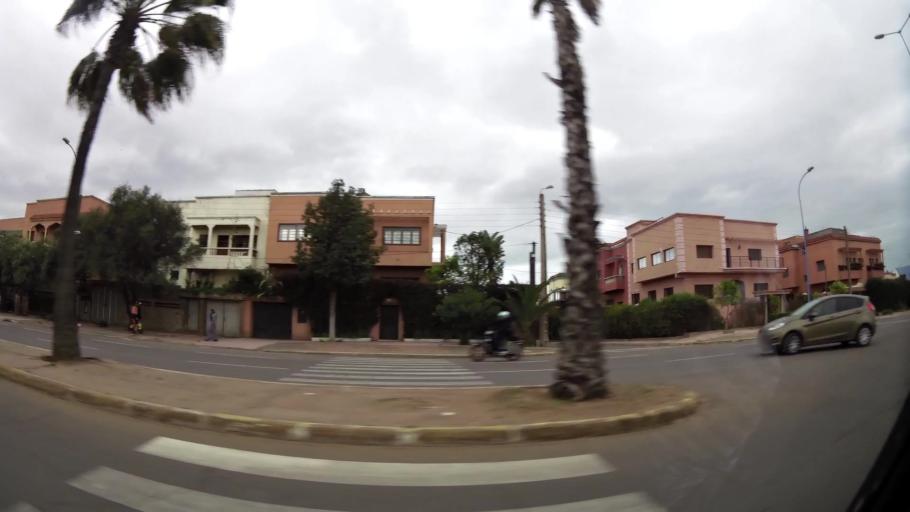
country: MA
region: Grand Casablanca
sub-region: Mediouna
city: Tit Mellil
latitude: 33.5637
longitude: -7.5317
